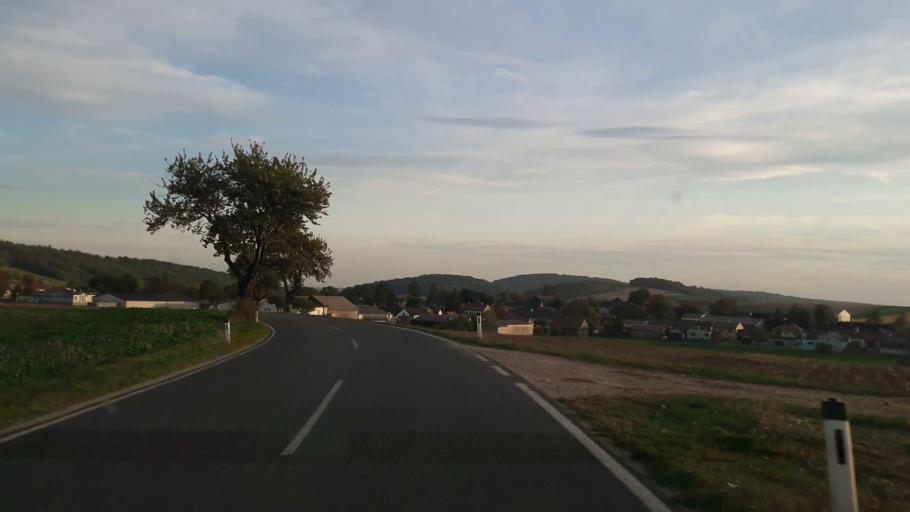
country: AT
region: Lower Austria
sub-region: Politischer Bezirk Korneuburg
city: Ernstbrunn
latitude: 48.5013
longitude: 16.3632
